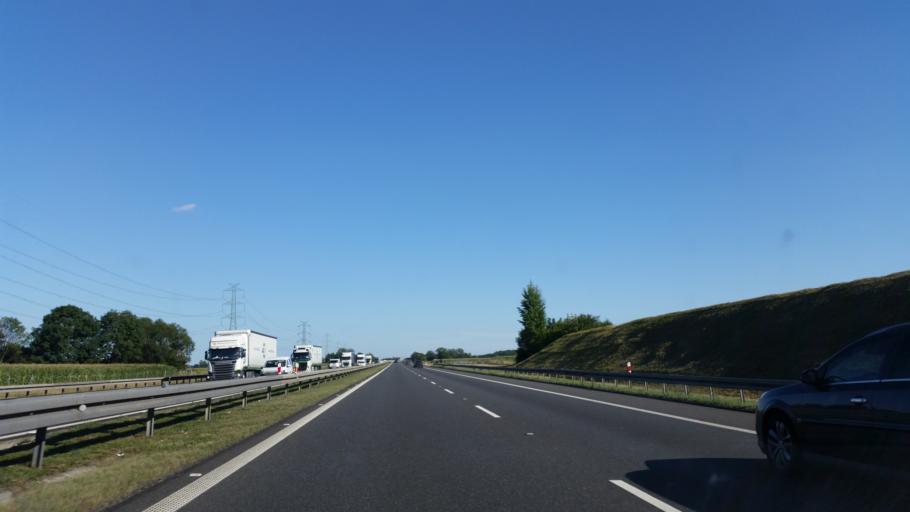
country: PL
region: Lower Silesian Voivodeship
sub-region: Powiat olawski
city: Wierzbno
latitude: 50.9273
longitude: 17.1241
